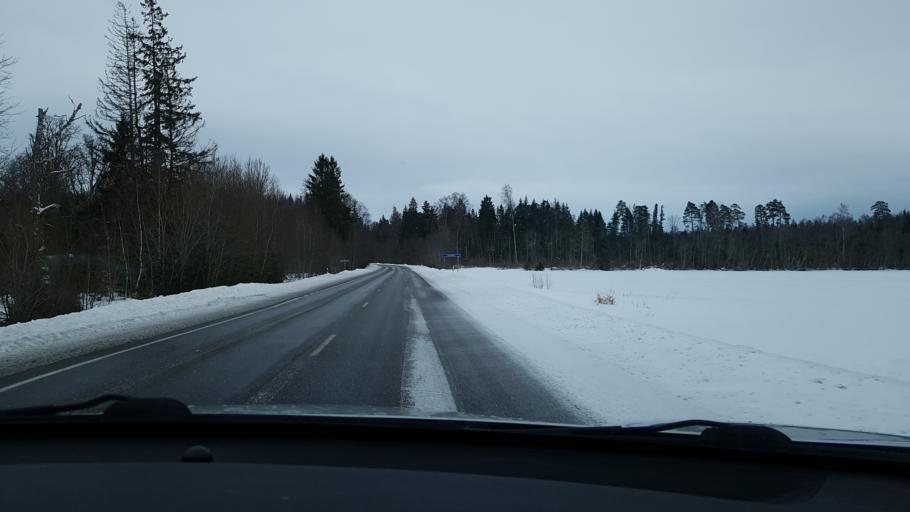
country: EE
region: Jaervamaa
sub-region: Jaerva-Jaani vald
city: Jarva-Jaani
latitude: 59.0997
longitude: 25.8173
